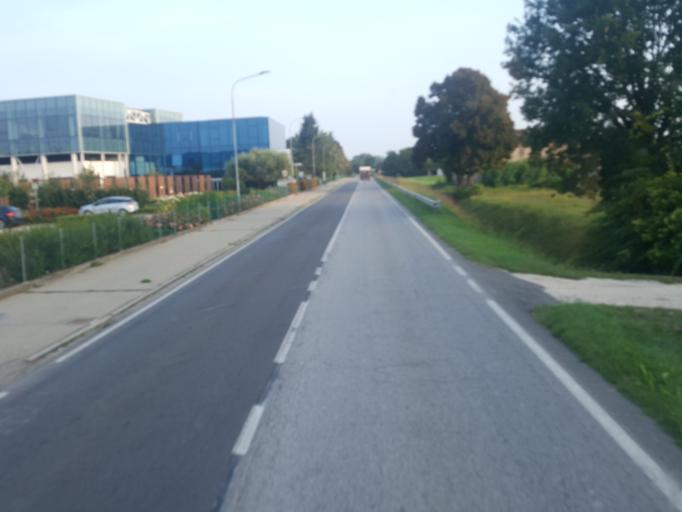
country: IT
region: Emilia-Romagna
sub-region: Provincia di Ravenna
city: Lavezzola
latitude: 44.5691
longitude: 11.8760
